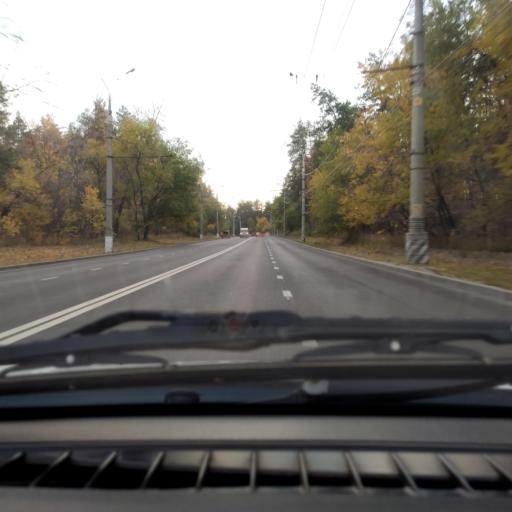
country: RU
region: Samara
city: Zhigulevsk
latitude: 53.4907
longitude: 49.4627
